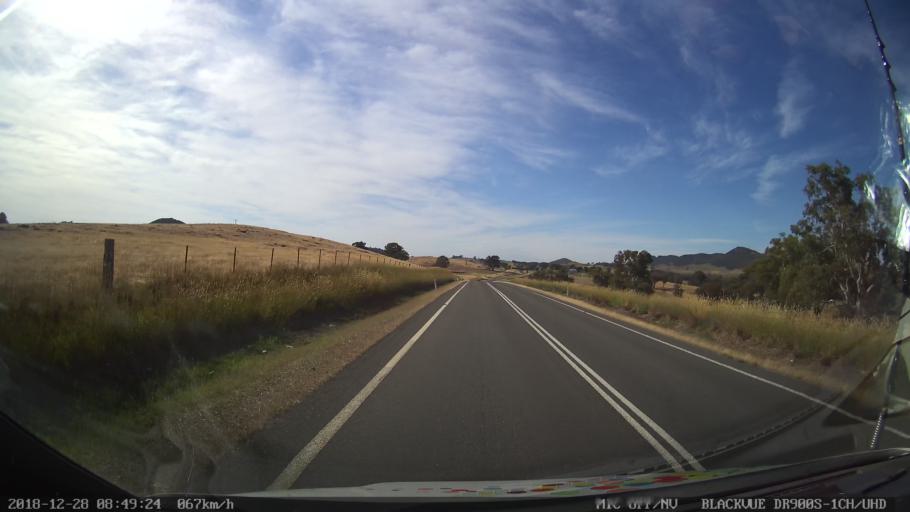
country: AU
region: New South Wales
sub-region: Upper Lachlan Shire
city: Crookwell
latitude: -34.0452
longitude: 149.3369
